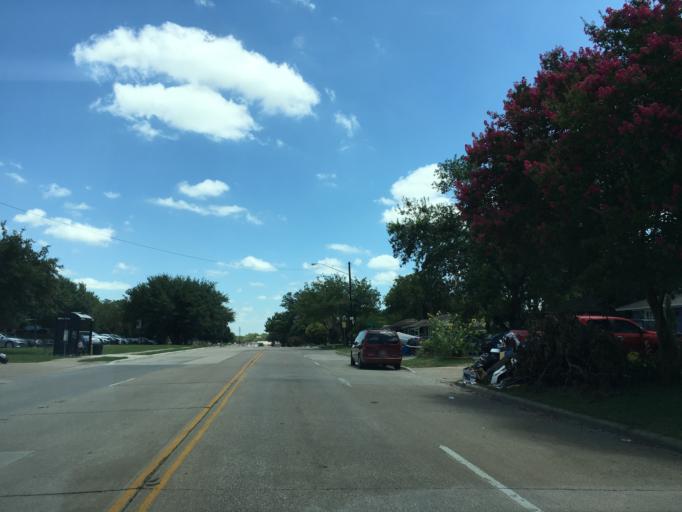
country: US
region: Texas
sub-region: Dallas County
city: Garland
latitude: 32.8428
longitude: -96.6701
